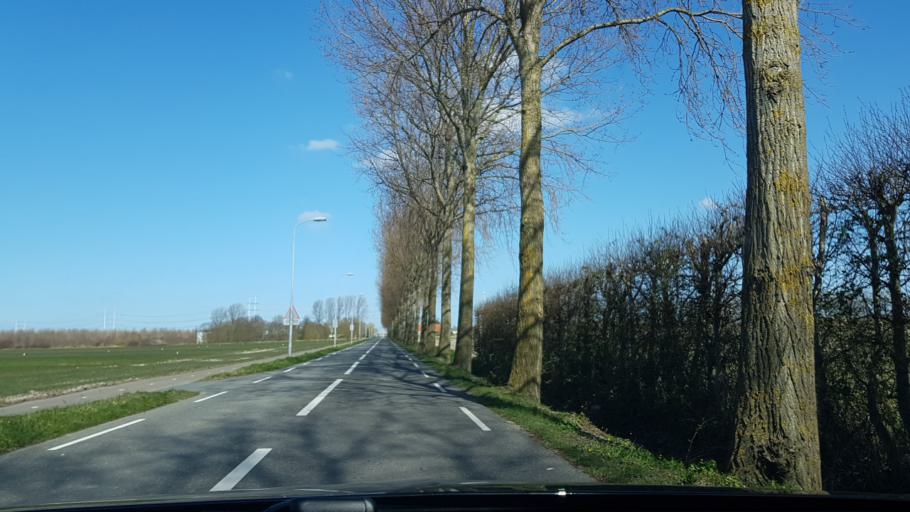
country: NL
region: South Holland
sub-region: Gemeente Lisse
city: Lisse
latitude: 52.2573
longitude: 4.5836
